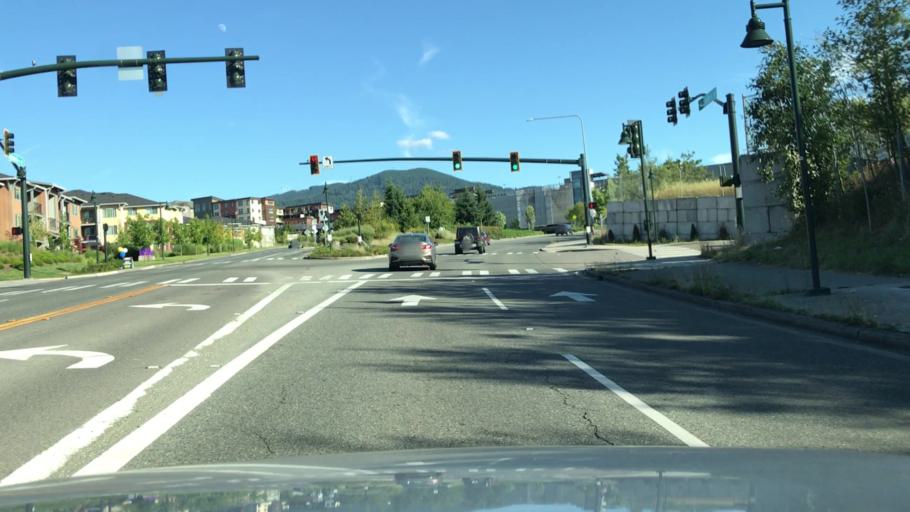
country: US
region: Washington
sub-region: King County
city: Issaquah
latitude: 47.5476
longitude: -122.0208
